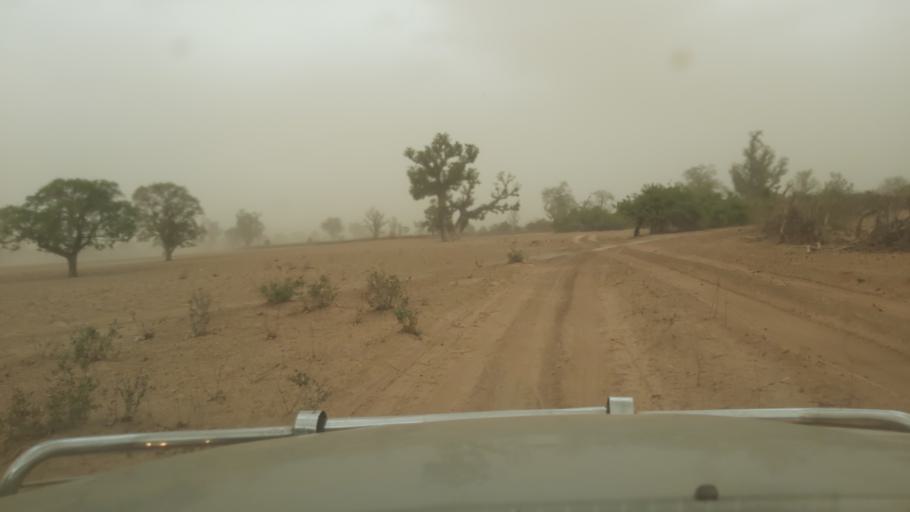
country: ML
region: Koulikoro
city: Banamba
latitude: 13.3779
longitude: -7.2047
